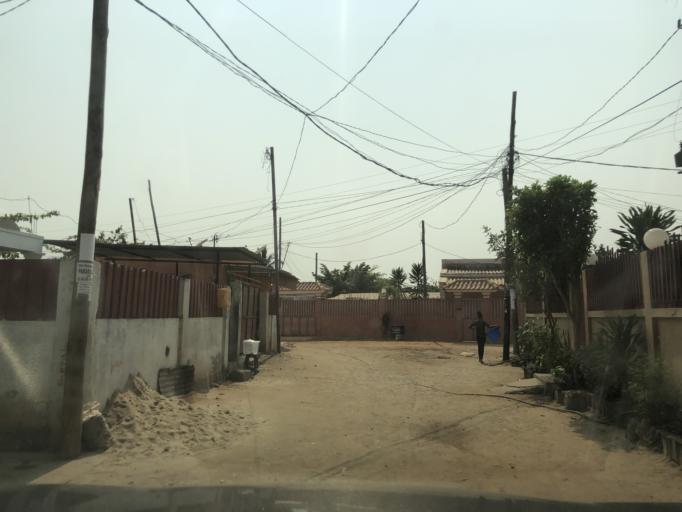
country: AO
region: Luanda
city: Luanda
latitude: -8.9033
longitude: 13.1663
